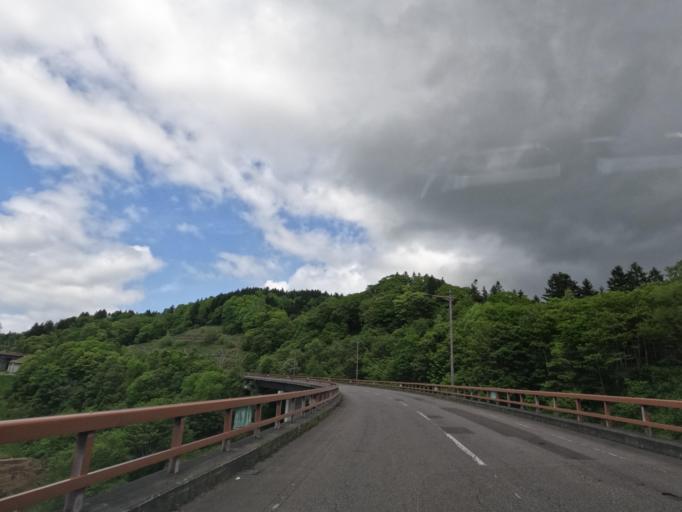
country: JP
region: Hokkaido
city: Tobetsu
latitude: 43.4757
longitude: 141.5957
